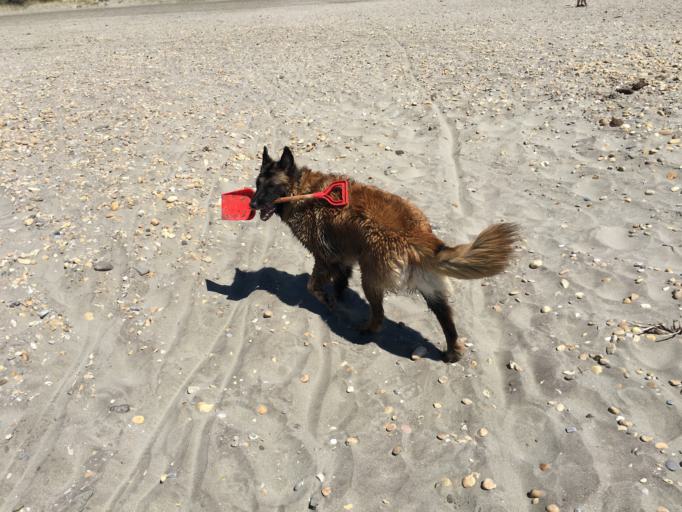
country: FR
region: Provence-Alpes-Cote d'Azur
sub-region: Departement des Bouches-du-Rhone
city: Saintes-Maries-de-la-Mer
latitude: 43.4584
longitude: 4.4579
